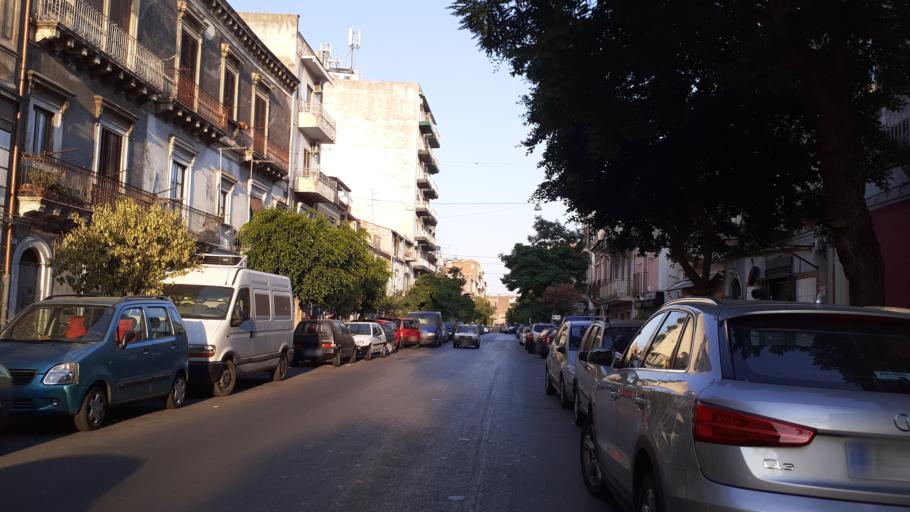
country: IT
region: Sicily
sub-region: Catania
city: Catania
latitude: 37.4985
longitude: 15.0806
